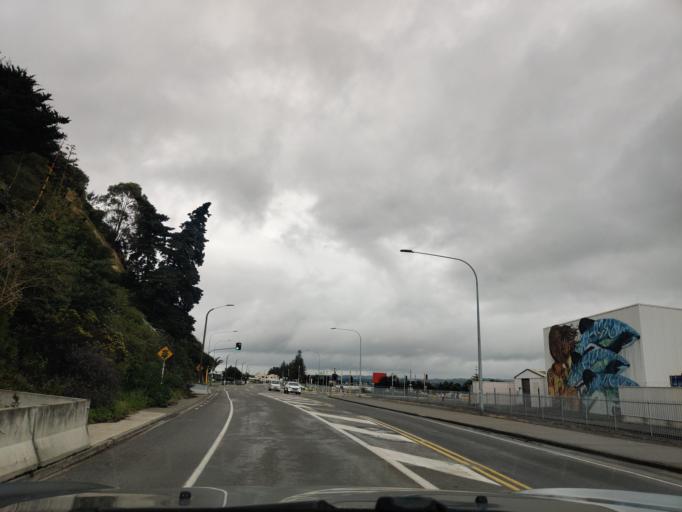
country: NZ
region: Hawke's Bay
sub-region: Napier City
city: Napier
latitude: -39.4776
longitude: 176.9126
